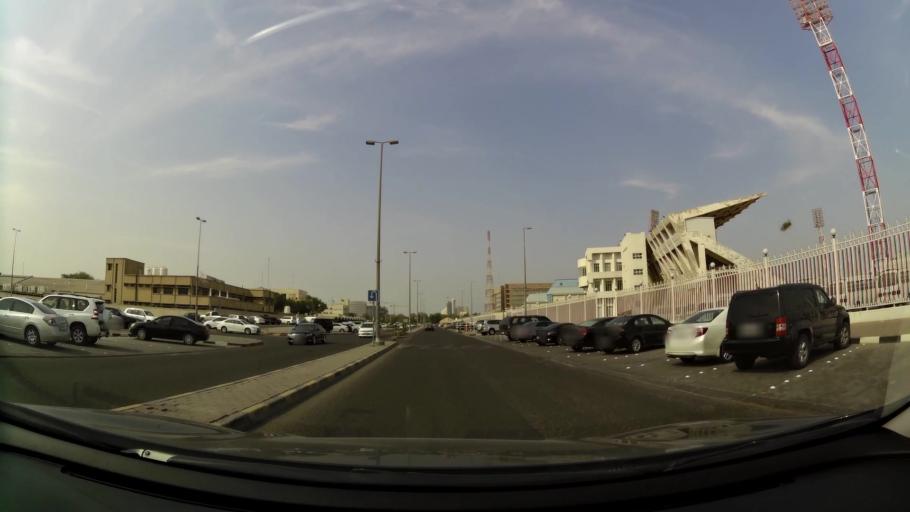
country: KW
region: Al Asimah
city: Ash Shamiyah
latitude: 29.3412
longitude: 47.9517
